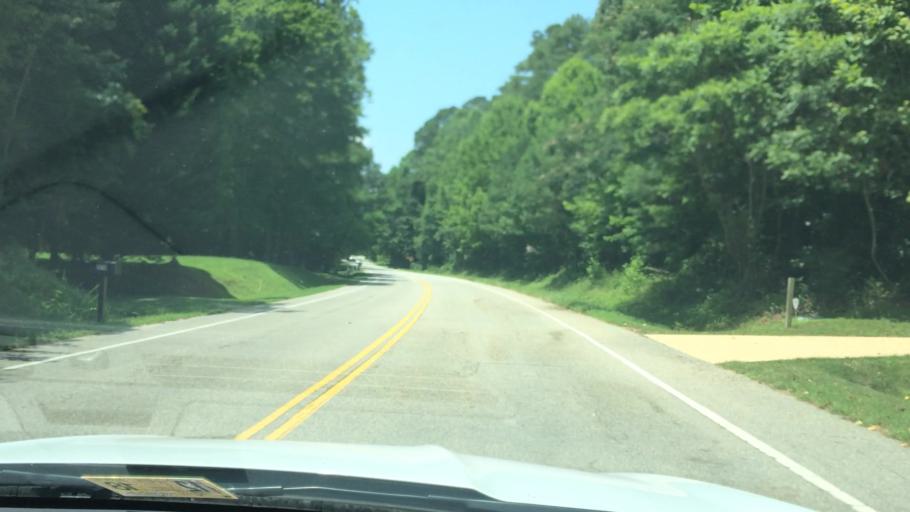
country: US
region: Virginia
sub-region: York County
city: Yorktown
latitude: 37.2055
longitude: -76.4941
